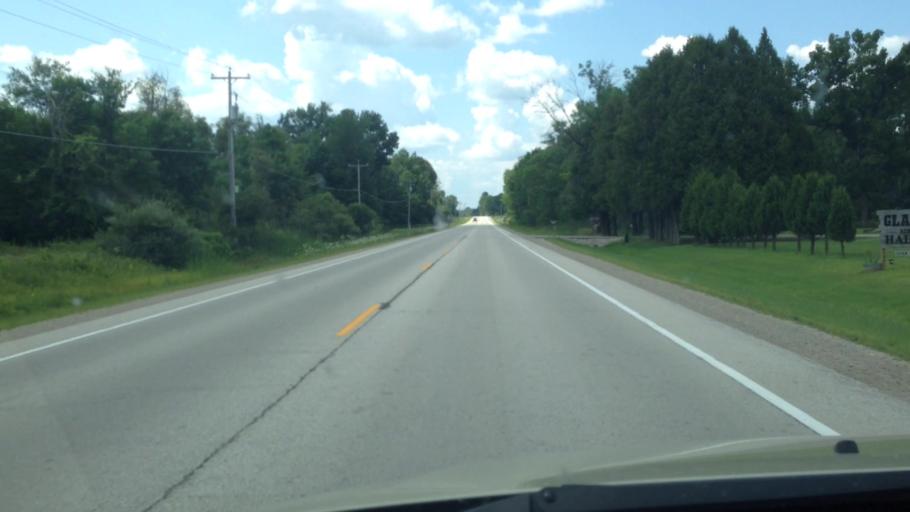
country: US
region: Wisconsin
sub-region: Brown County
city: Suamico
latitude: 44.6405
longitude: -88.0770
